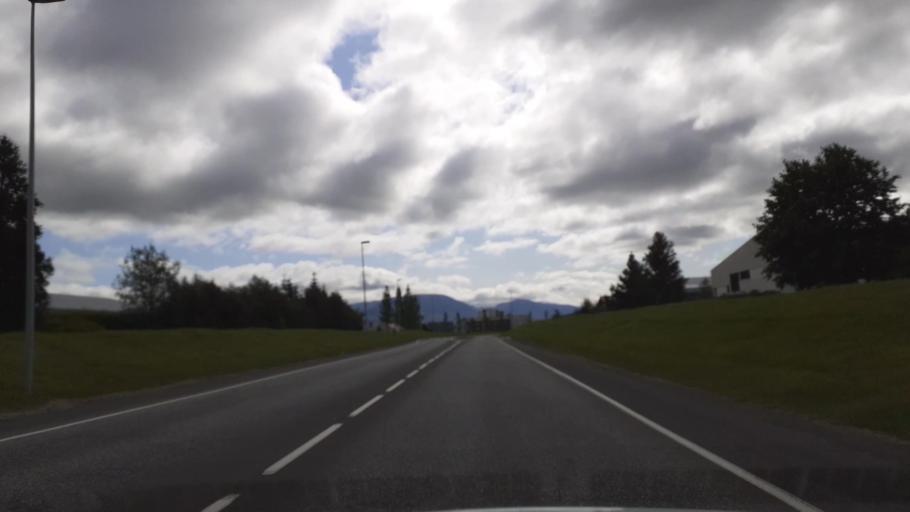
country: IS
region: Northeast
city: Akureyri
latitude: 65.6725
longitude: -18.1084
